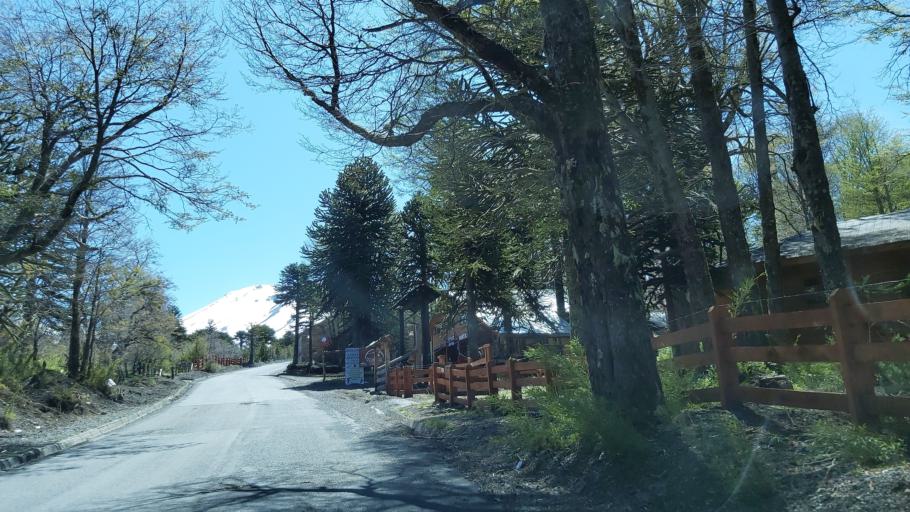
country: CL
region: Araucania
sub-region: Provincia de Cautin
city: Vilcun
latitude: -38.4346
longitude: -71.5346
